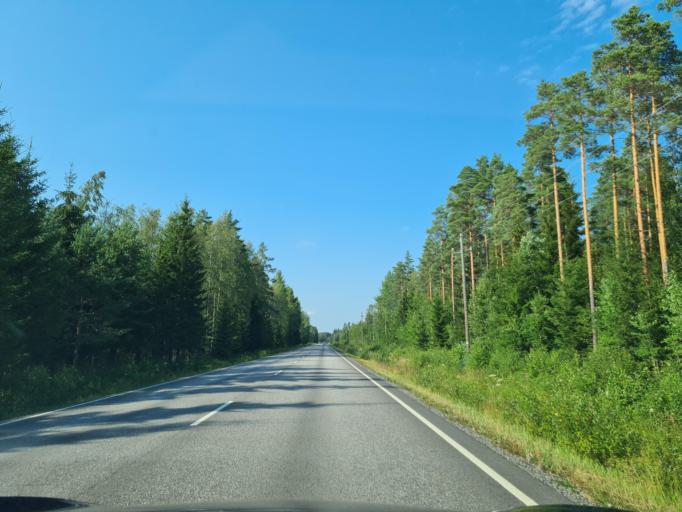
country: FI
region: Satakunta
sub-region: Pohjois-Satakunta
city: Kankaanpaeae
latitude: 61.9268
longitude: 22.5076
